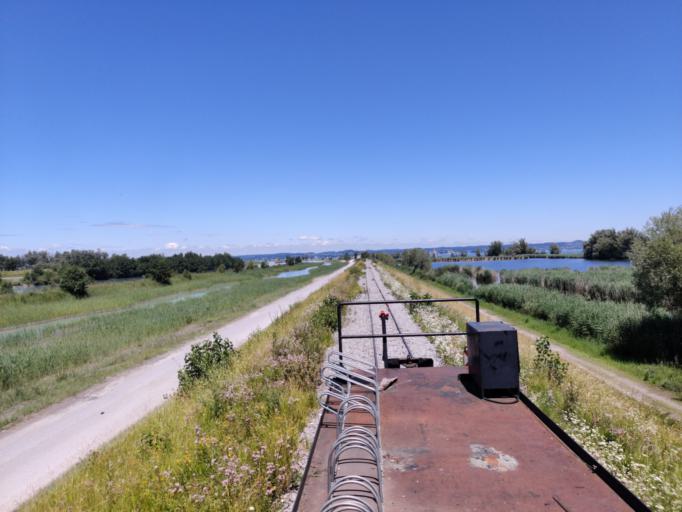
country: AT
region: Vorarlberg
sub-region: Politischer Bezirk Bregenz
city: Hard
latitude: 47.4920
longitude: 9.6719
